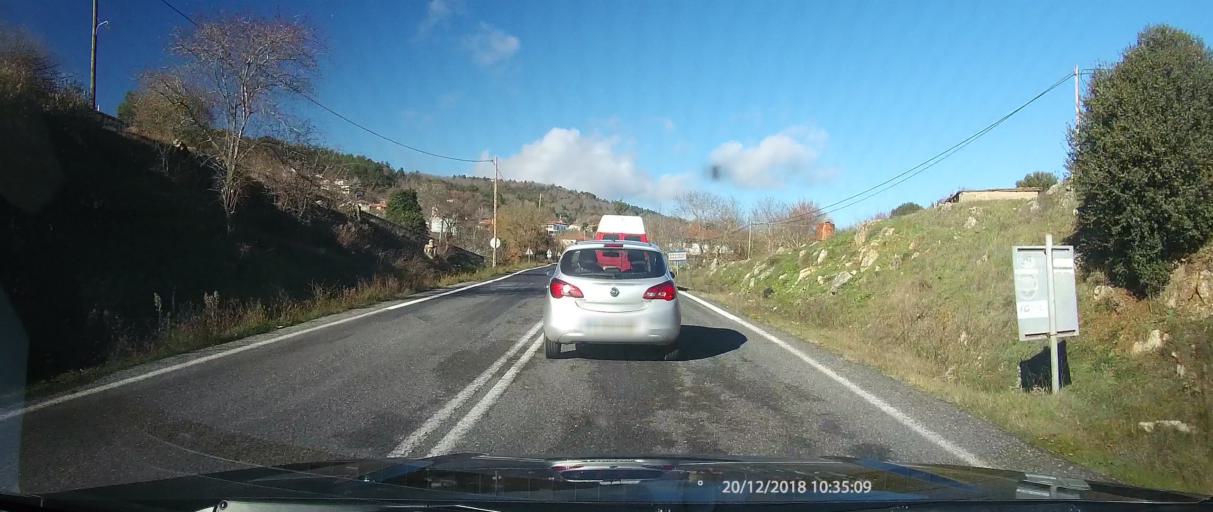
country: GR
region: Peloponnese
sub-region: Nomos Lakonias
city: Kariai
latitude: 37.3545
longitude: 22.4129
